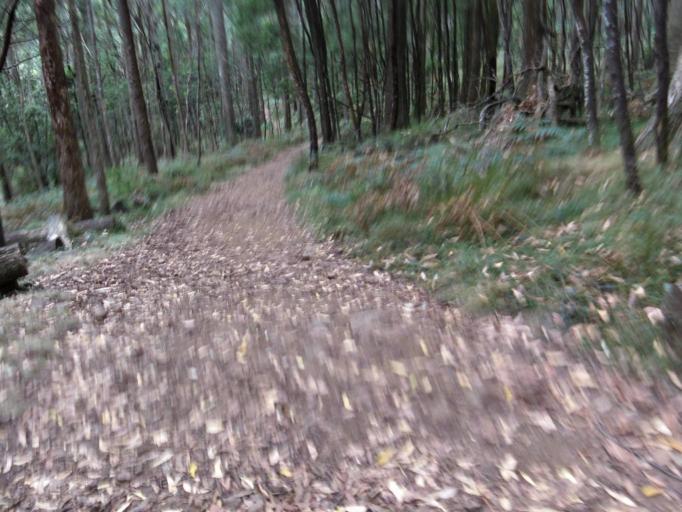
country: AU
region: Victoria
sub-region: Hume
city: Sunbury
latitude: -37.3778
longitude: 144.5753
